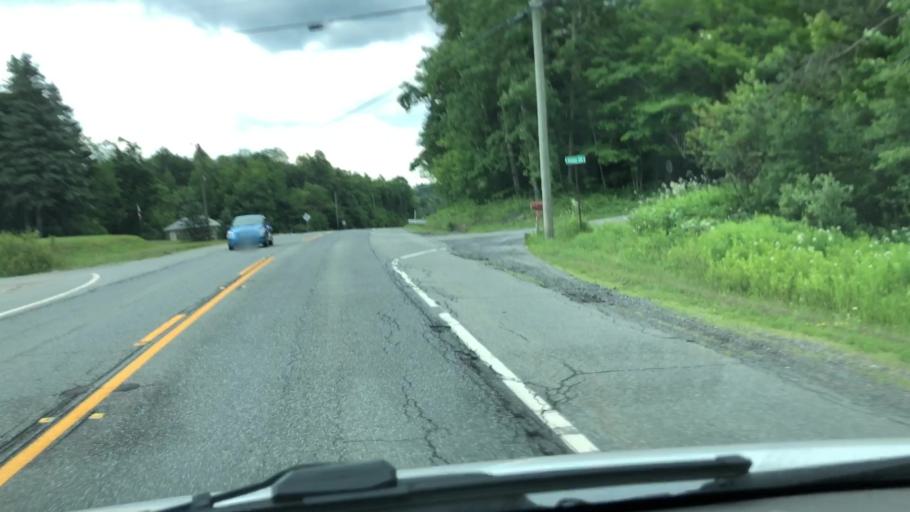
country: US
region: Massachusetts
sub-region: Berkshire County
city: Hinsdale
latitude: 42.5090
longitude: -73.0461
